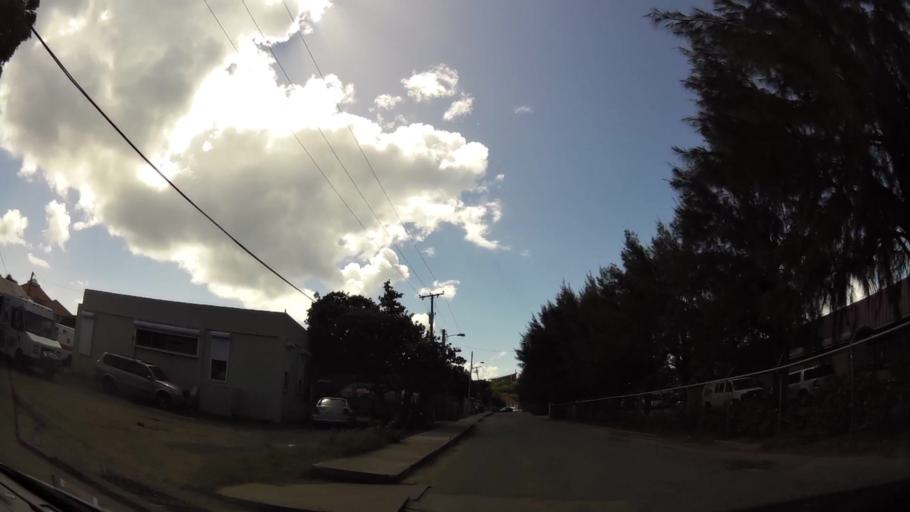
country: VG
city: Tortola
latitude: 18.4500
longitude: -64.4352
